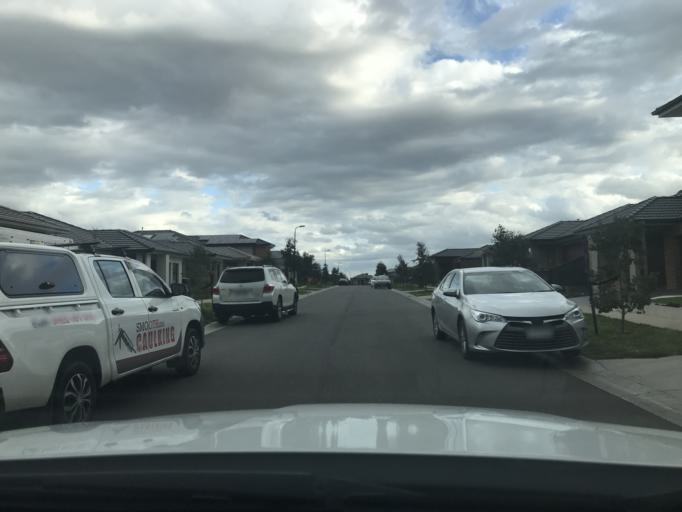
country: AU
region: Victoria
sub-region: Hume
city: Roxburgh Park
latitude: -37.5848
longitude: 144.8922
